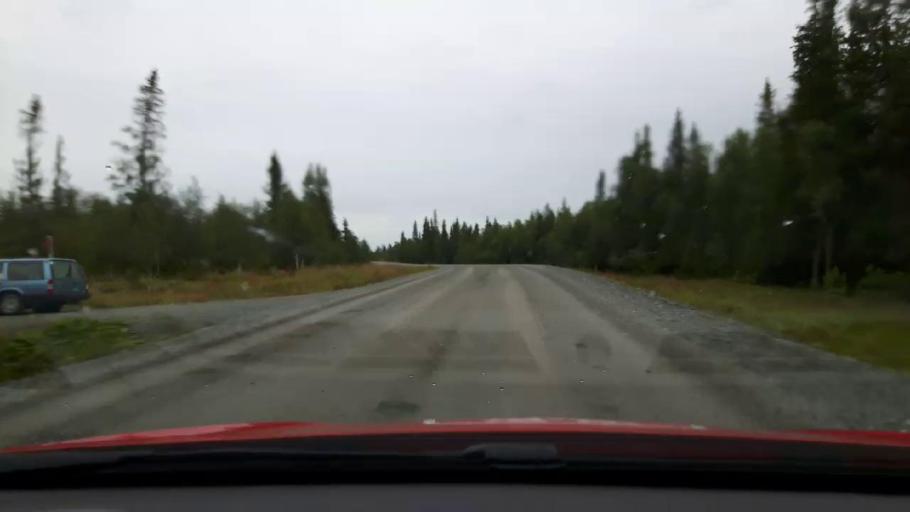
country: SE
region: Jaemtland
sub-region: Are Kommun
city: Are
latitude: 63.5151
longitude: 12.4149
